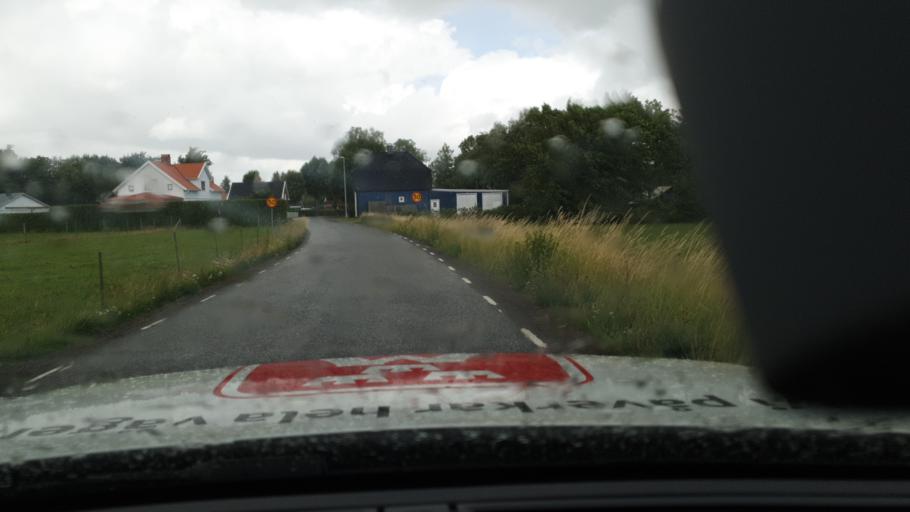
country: SE
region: Vaestra Goetaland
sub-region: Falkopings Kommun
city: Akarp
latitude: 58.2215
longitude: 13.6050
